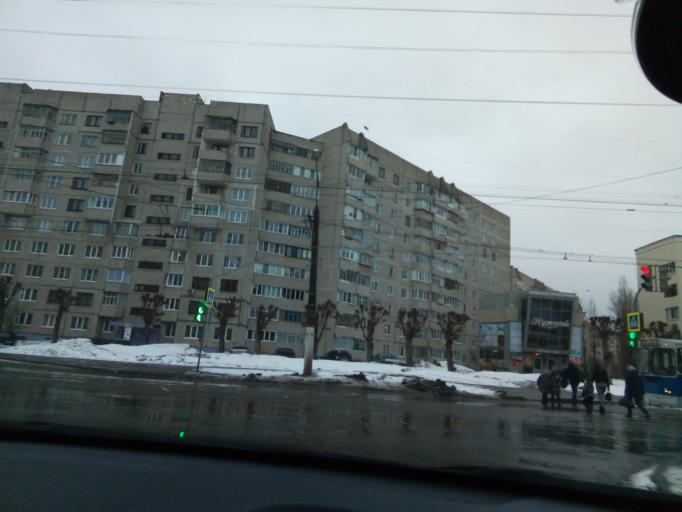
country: RU
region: Chuvashia
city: Novyye Lapsary
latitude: 56.1140
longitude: 47.1867
